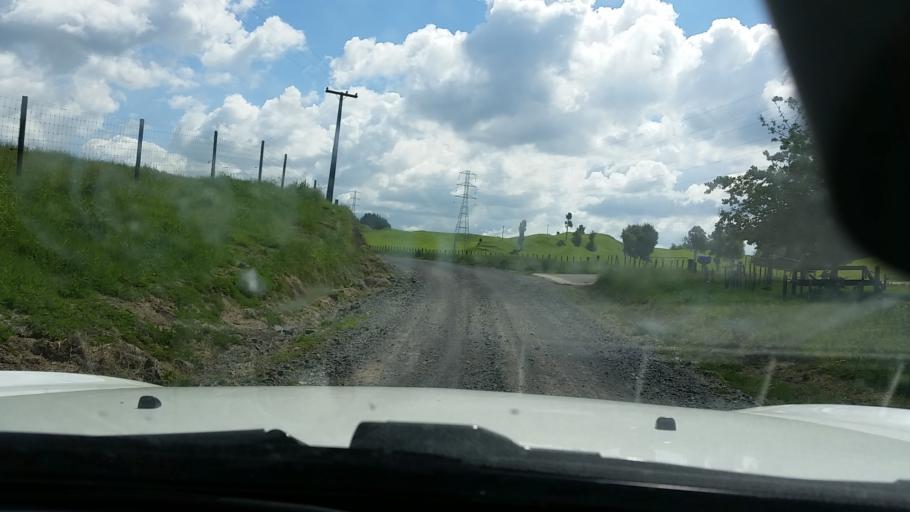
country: NZ
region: Bay of Plenty
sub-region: Rotorua District
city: Rotorua
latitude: -38.0085
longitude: 176.1975
